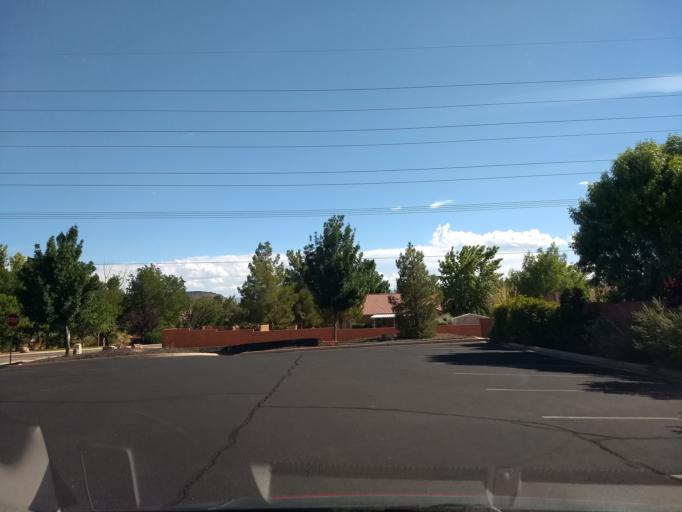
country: US
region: Utah
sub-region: Washington County
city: Santa Clara
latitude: 37.1324
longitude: -113.6141
